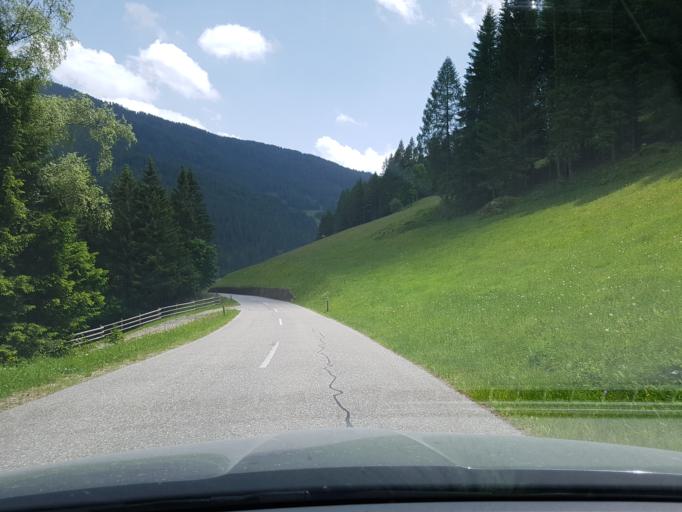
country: AT
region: Carinthia
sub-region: Politischer Bezirk Spittal an der Drau
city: Kleinkirchheim
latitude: 46.8727
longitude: 13.8749
